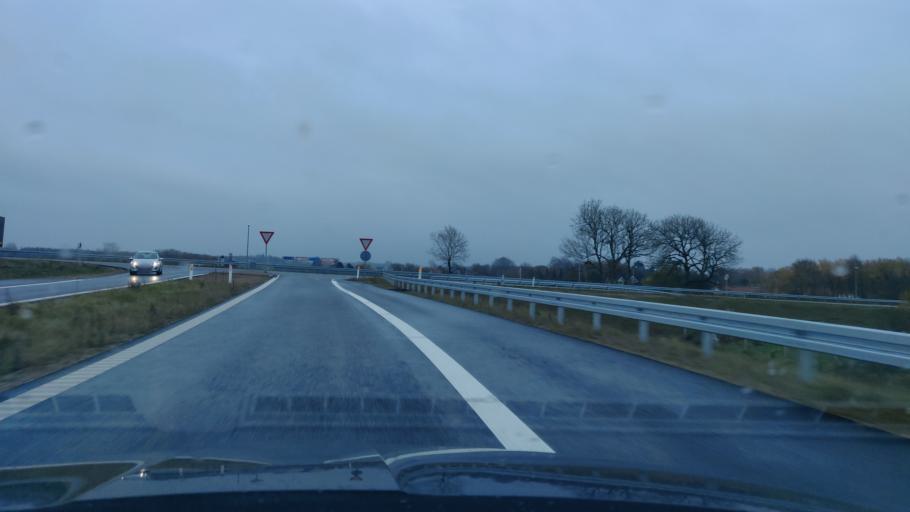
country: DK
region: Central Jutland
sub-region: Herning Kommune
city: Avlum
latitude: 56.2184
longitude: 8.8478
